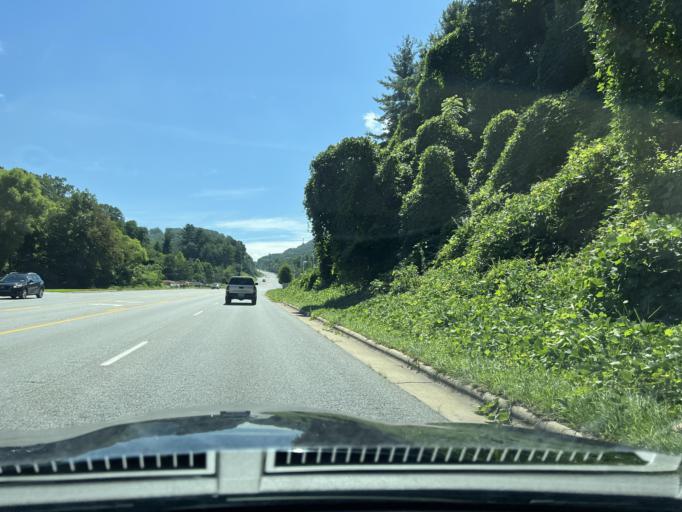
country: US
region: North Carolina
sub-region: Buncombe County
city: Biltmore Forest
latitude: 35.5508
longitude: -82.4715
